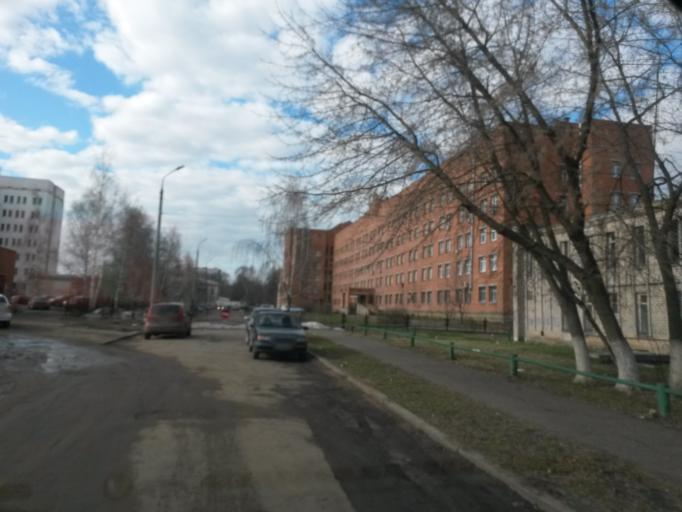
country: RU
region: Jaroslavl
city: Yaroslavl
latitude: 57.6329
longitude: 39.8397
